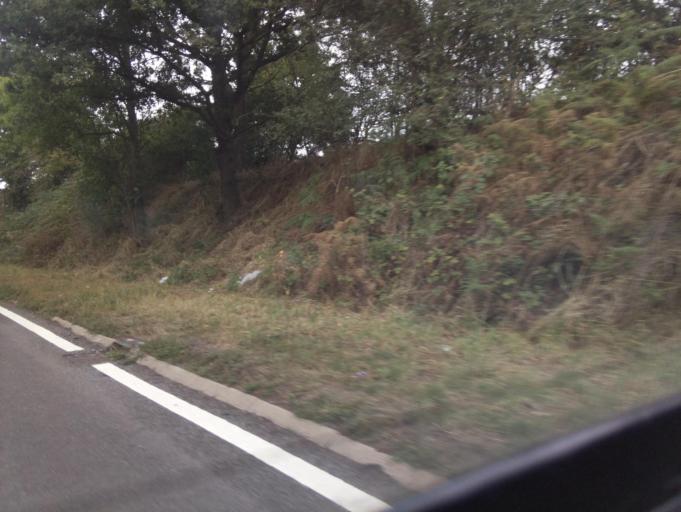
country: GB
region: England
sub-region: Shropshire
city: Bridgnorth
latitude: 52.5677
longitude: -2.3922
